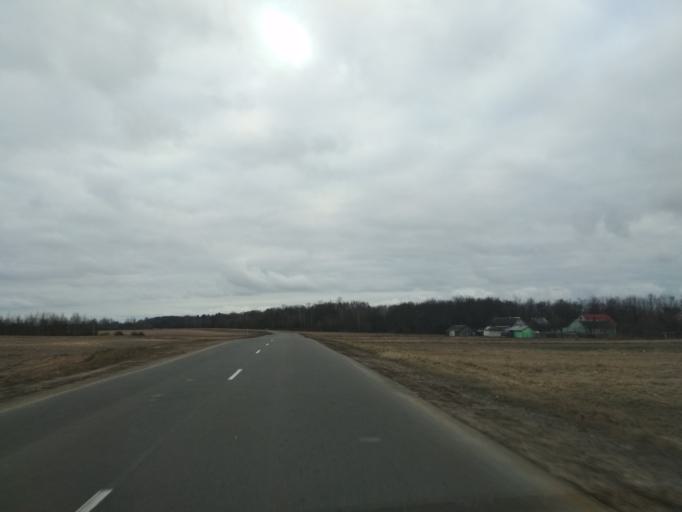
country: BY
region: Minsk
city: Druzhny
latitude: 53.5781
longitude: 27.9238
